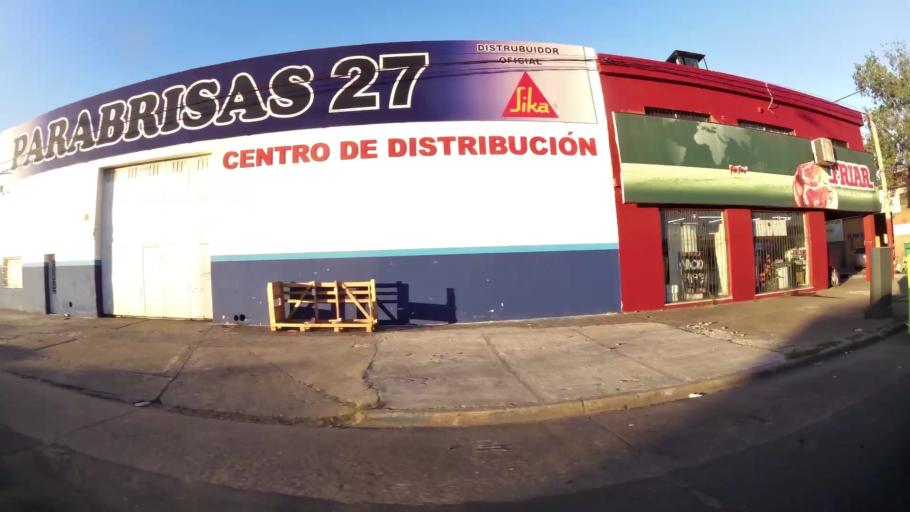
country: AR
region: Santa Fe
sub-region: Departamento de Rosario
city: Rosario
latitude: -32.9619
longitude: -60.6753
